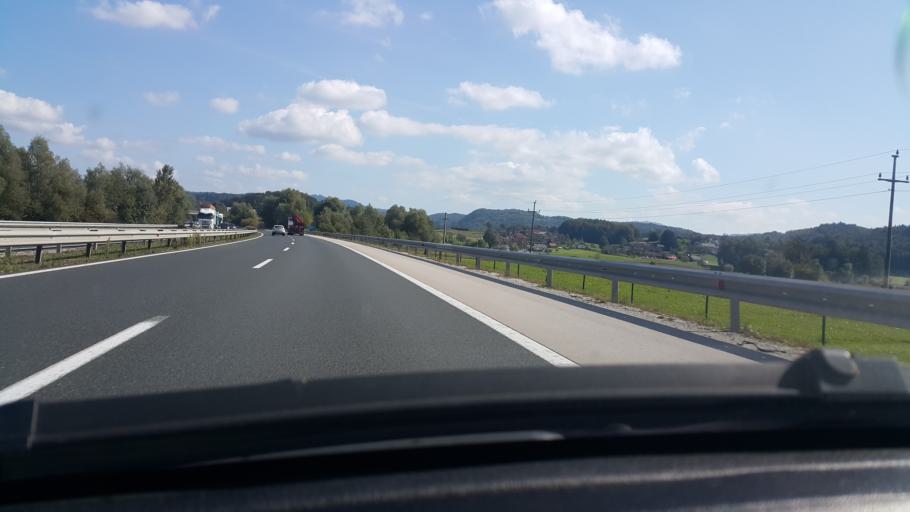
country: SI
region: Lukovica
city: Lukovica pri Domzalah
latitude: 46.1547
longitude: 14.6654
